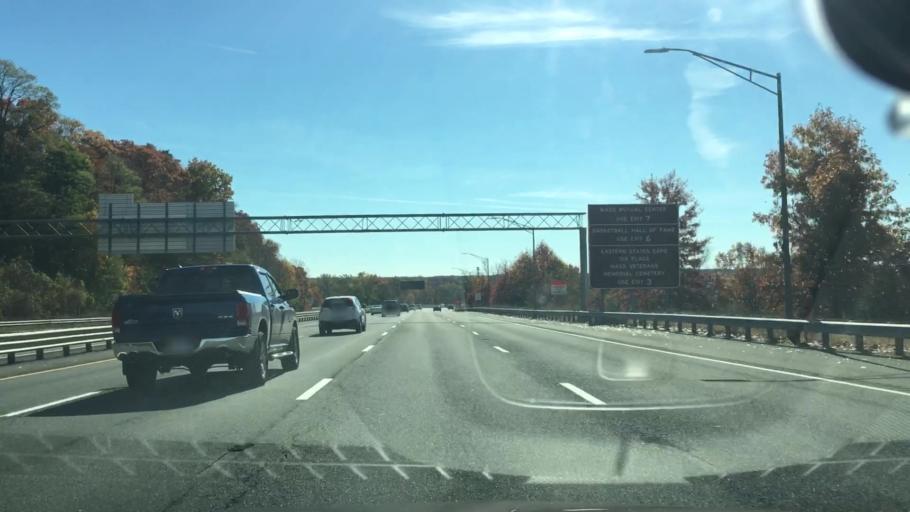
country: US
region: Massachusetts
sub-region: Hampden County
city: Chicopee
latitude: 42.1269
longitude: -72.6084
